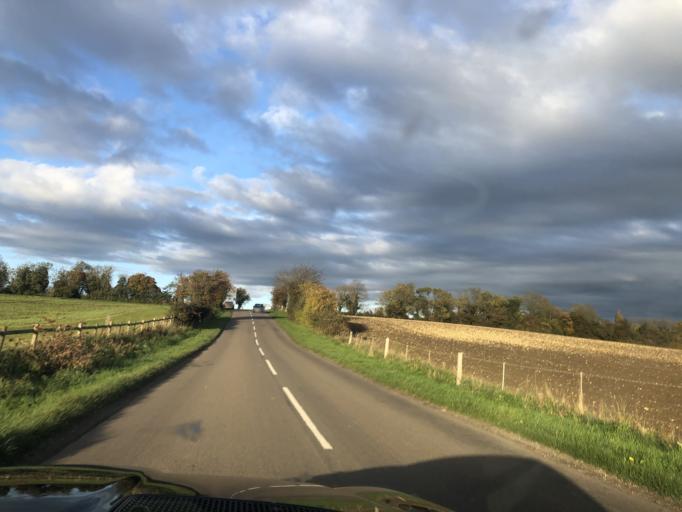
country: GB
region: England
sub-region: Warwickshire
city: Harbury
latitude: 52.2313
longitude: -1.4881
